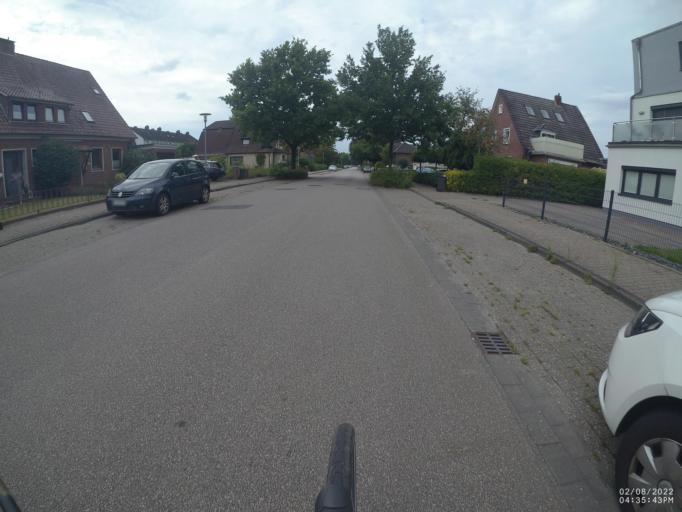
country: DE
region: Lower Saxony
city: Oldenburg
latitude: 53.1645
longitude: 8.1953
